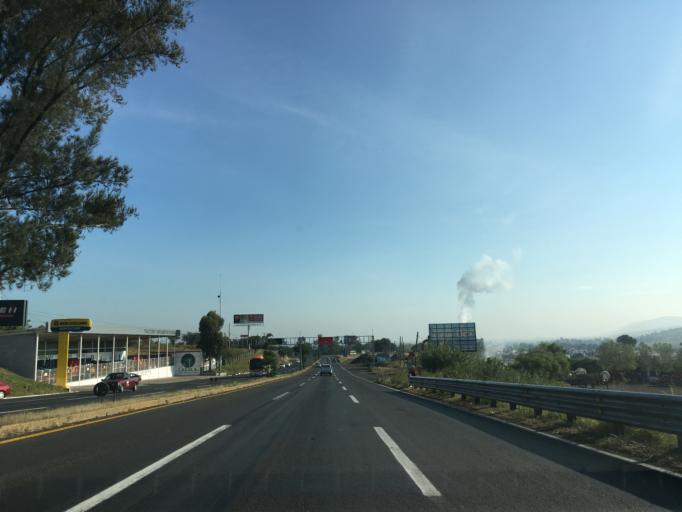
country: MX
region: Michoacan
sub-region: Tarimbaro
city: San Bernabe de las Canteras
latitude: 19.7644
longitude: -101.1624
